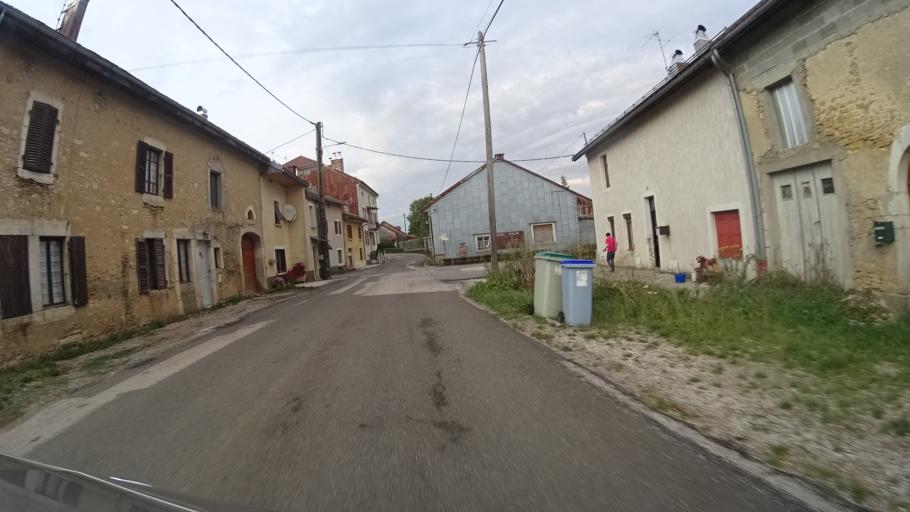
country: FR
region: Franche-Comte
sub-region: Departement du Jura
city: Morbier
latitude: 46.6192
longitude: 5.9927
